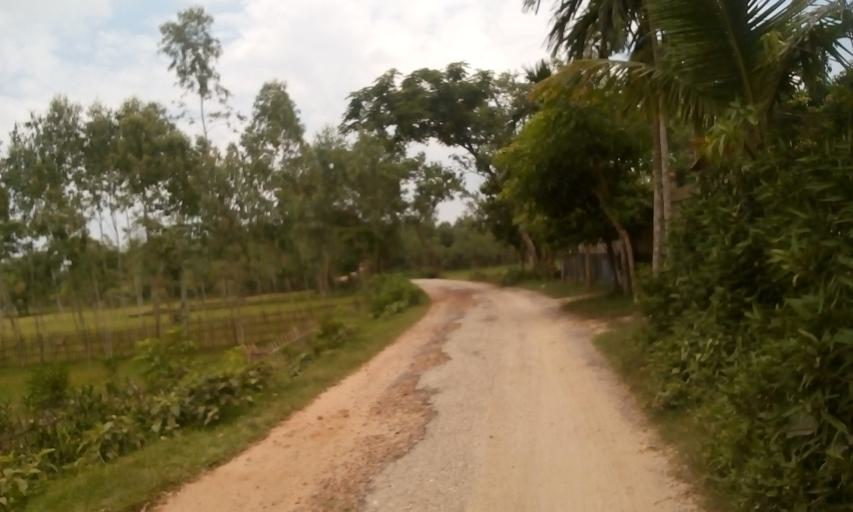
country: BD
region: Rangpur Division
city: Parbatipur
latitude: 25.3993
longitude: 88.9856
